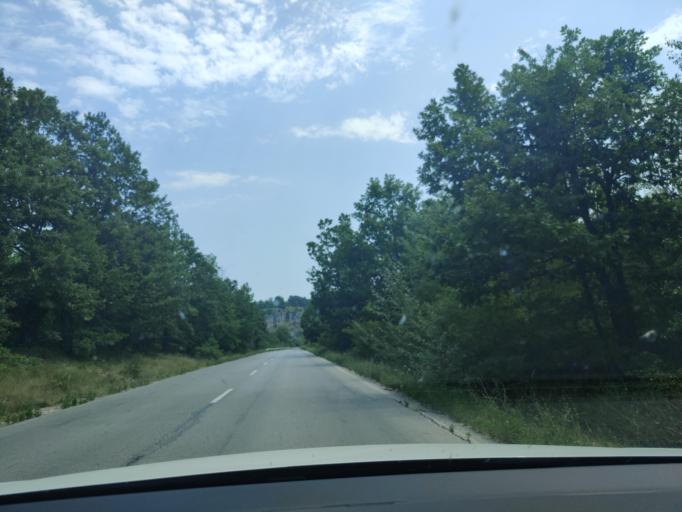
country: BG
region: Vidin
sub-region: Obshtina Ruzhintsi
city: Ruzhintsi
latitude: 43.5684
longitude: 22.9100
